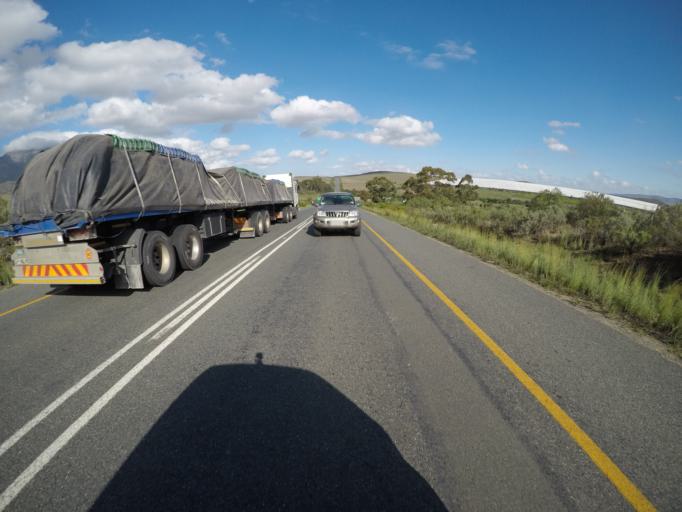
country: ZA
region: Western Cape
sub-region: Overberg District Municipality
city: Swellendam
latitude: -33.9594
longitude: 20.2391
